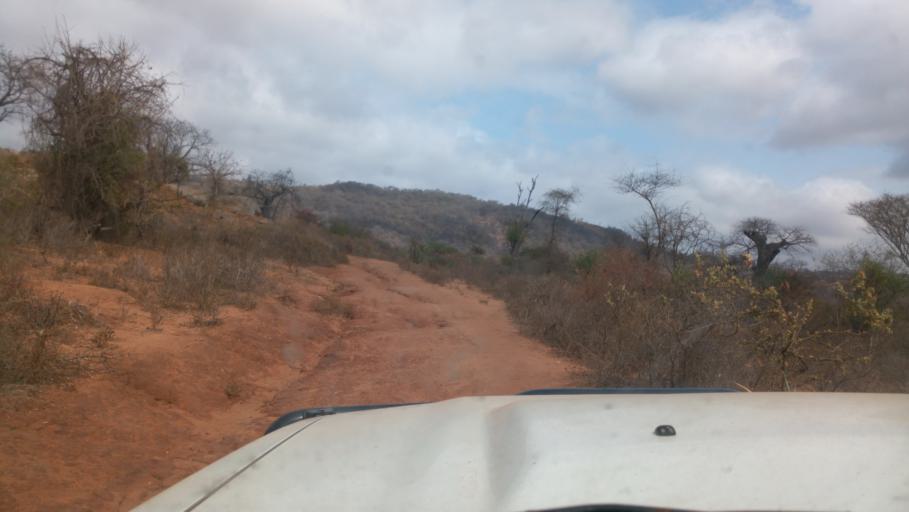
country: KE
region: Kitui
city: Kitui
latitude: -1.8396
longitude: 38.2998
